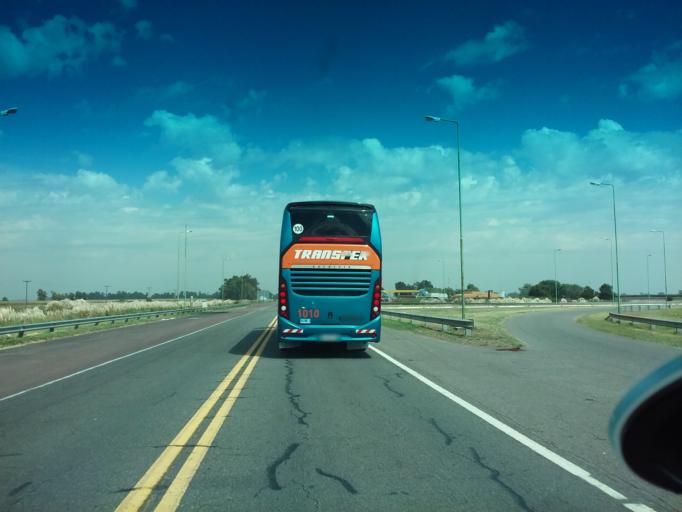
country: AR
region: Buenos Aires
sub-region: Partido de Carlos Casares
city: Carlos Casares
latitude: -35.6560
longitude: -61.3964
